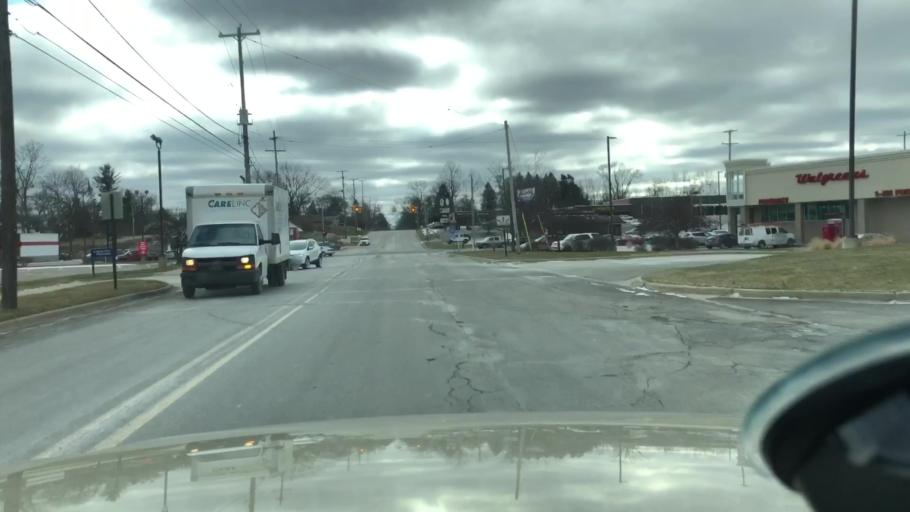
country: US
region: Michigan
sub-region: Jackson County
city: Jackson
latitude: 42.2568
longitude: -84.3650
